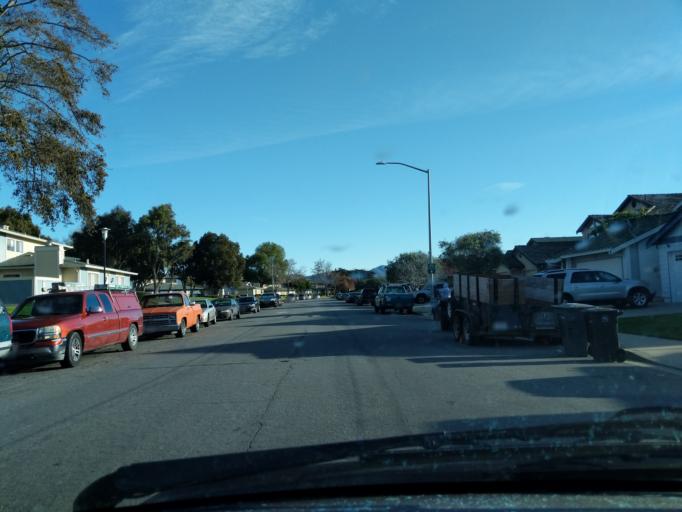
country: US
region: California
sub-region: Monterey County
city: Boronda
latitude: 36.7106
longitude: -121.6573
